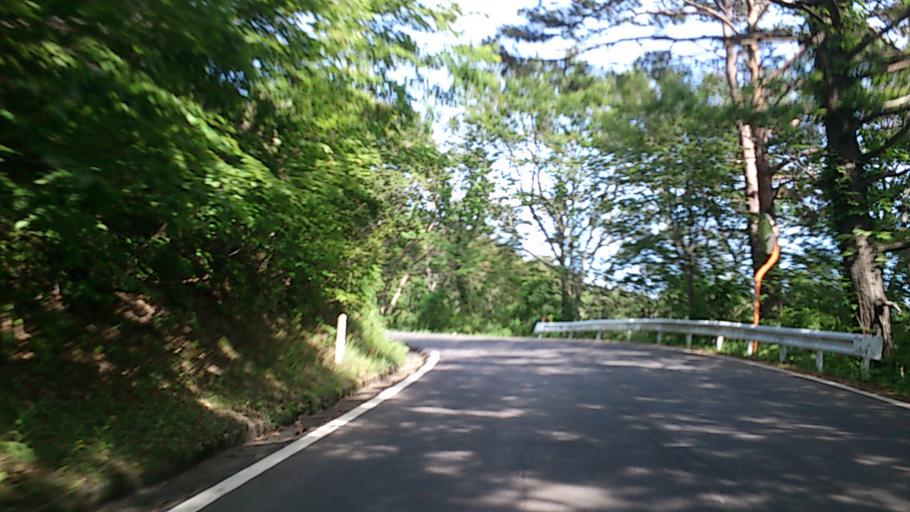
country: JP
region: Aomori
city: Aomori Shi
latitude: 40.7147
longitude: 140.8192
